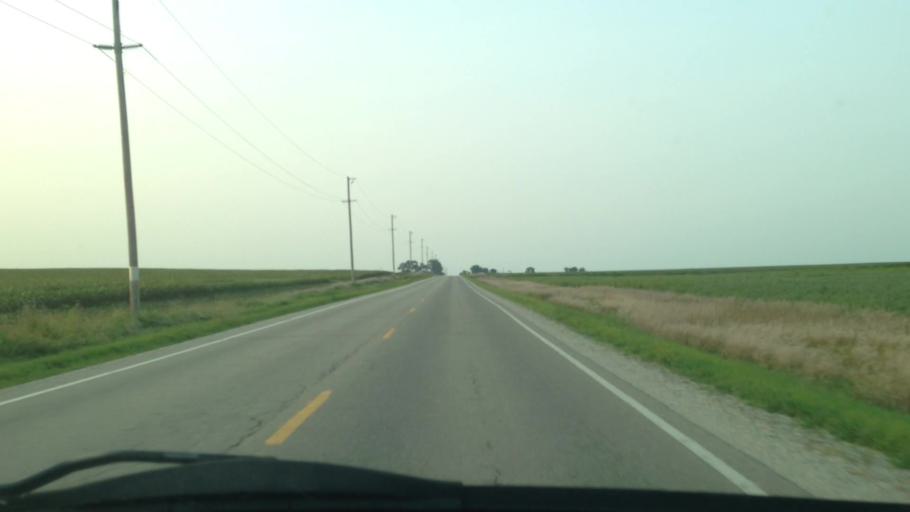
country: US
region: Iowa
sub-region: Iowa County
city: Marengo
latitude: 41.9542
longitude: -92.0852
